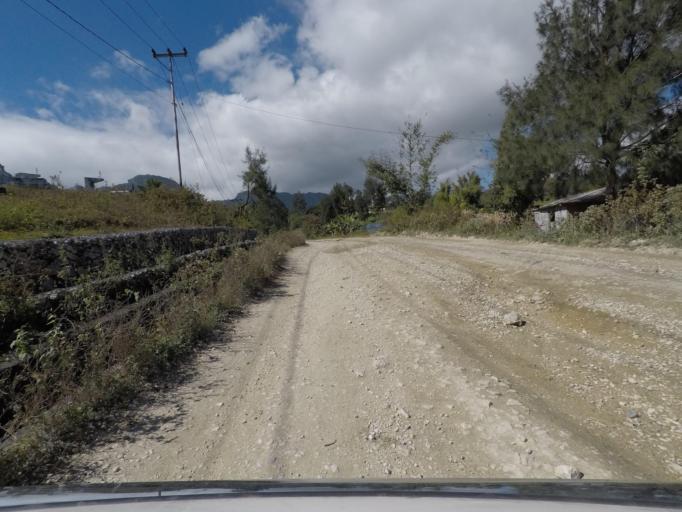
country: TL
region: Baucau
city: Venilale
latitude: -8.6753
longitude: 126.3710
